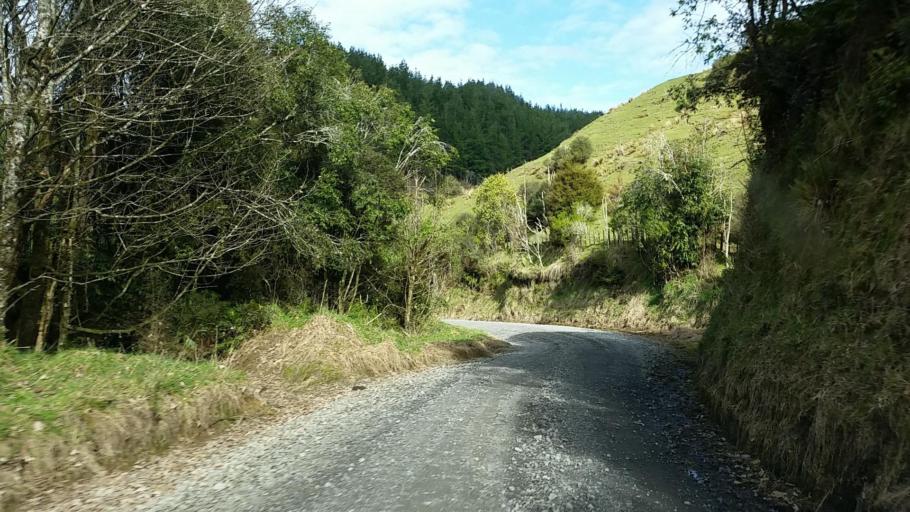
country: NZ
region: Taranaki
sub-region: New Plymouth District
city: Waitara
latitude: -39.1525
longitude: 174.5586
